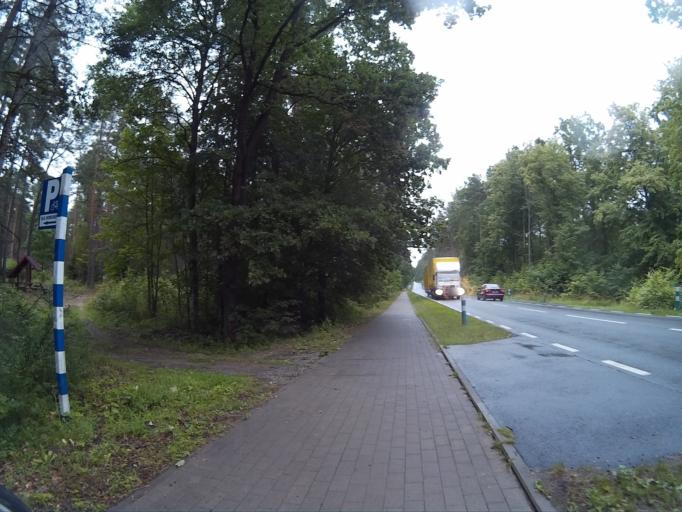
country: PL
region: Kujawsko-Pomorskie
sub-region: Powiat swiecki
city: Osie
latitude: 53.6095
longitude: 18.3037
